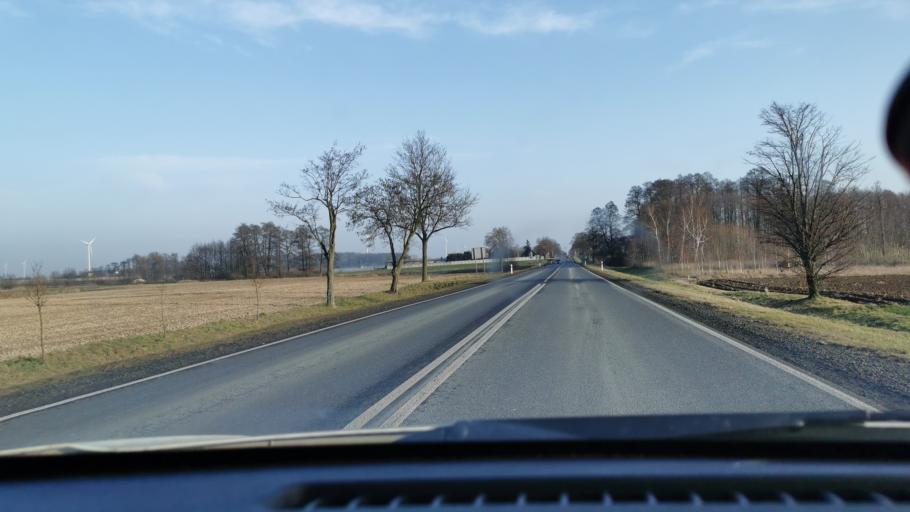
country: PL
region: Lodz Voivodeship
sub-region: Powiat sieradzki
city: Blaszki
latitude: 51.6417
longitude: 18.4946
